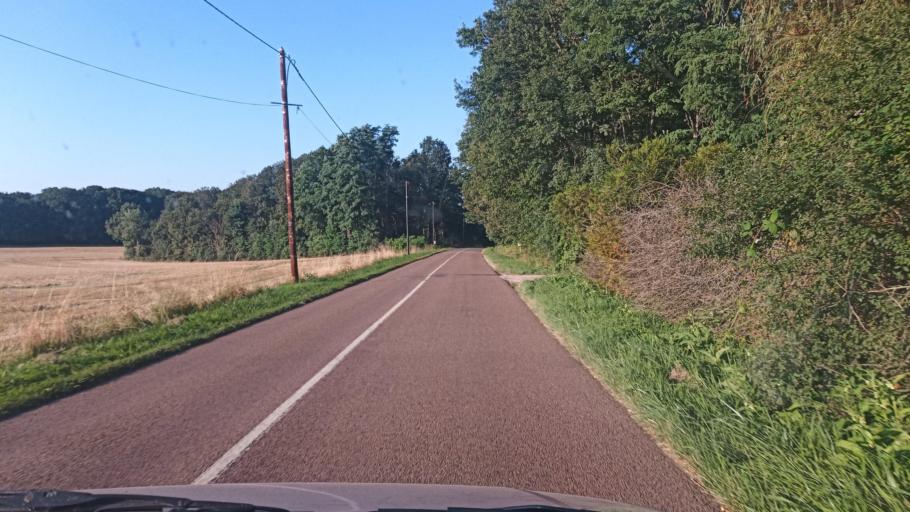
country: FR
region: Bourgogne
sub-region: Departement de l'Yonne
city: Pont-sur-Yonne
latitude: 48.2565
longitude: 3.1707
